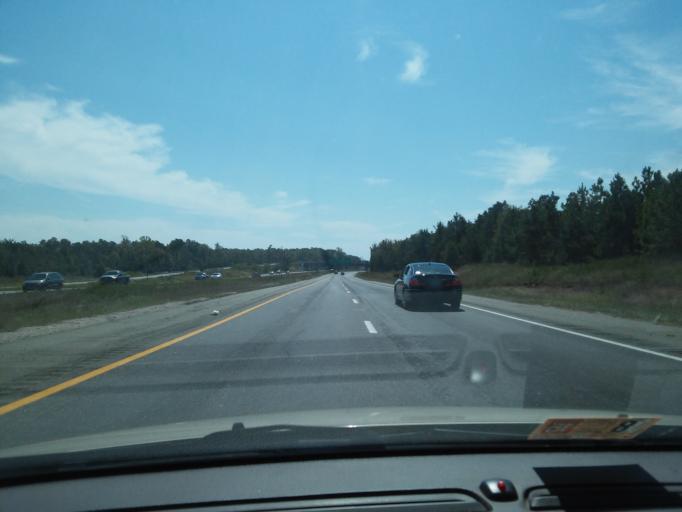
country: US
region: Virginia
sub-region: Henrico County
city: Short Pump
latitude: 37.6424
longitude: -77.6653
